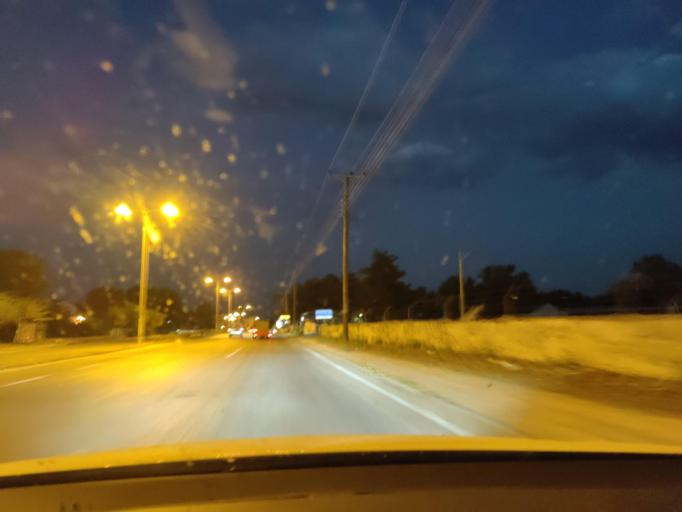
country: GR
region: Central Macedonia
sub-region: Nomos Serron
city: Serres
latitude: 41.0878
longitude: 23.5256
